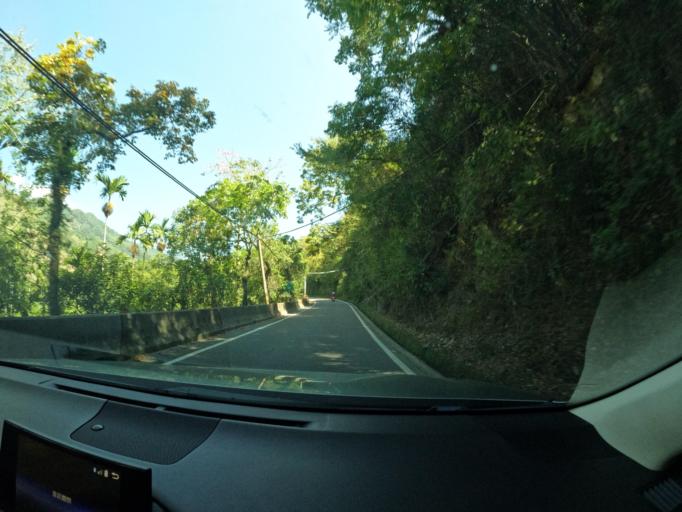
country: TW
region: Taiwan
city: Yujing
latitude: 23.2348
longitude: 120.8122
